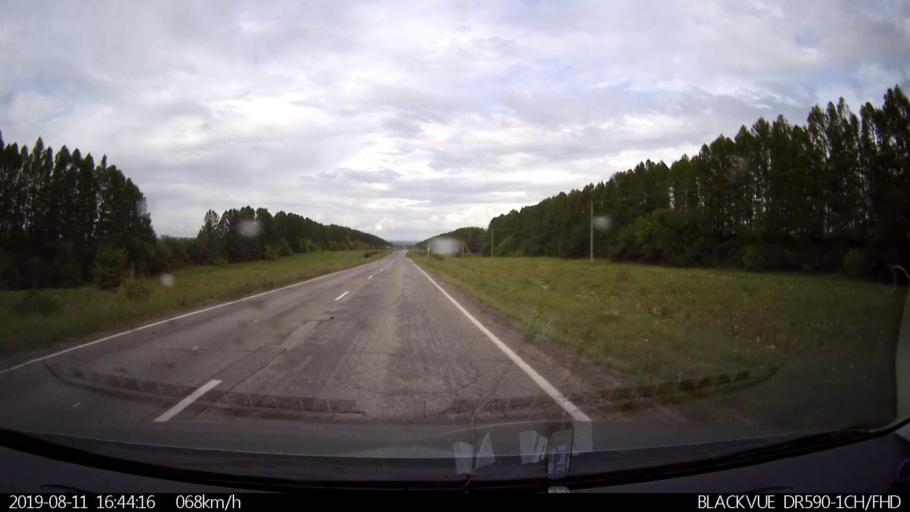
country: RU
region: Ulyanovsk
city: Mayna
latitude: 54.1772
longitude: 47.6788
